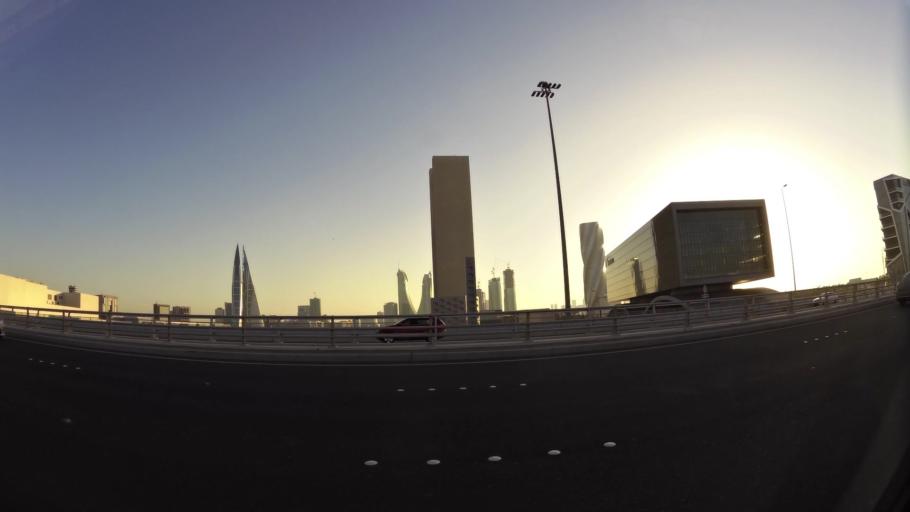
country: BH
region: Muharraq
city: Al Muharraq
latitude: 26.2505
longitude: 50.5853
